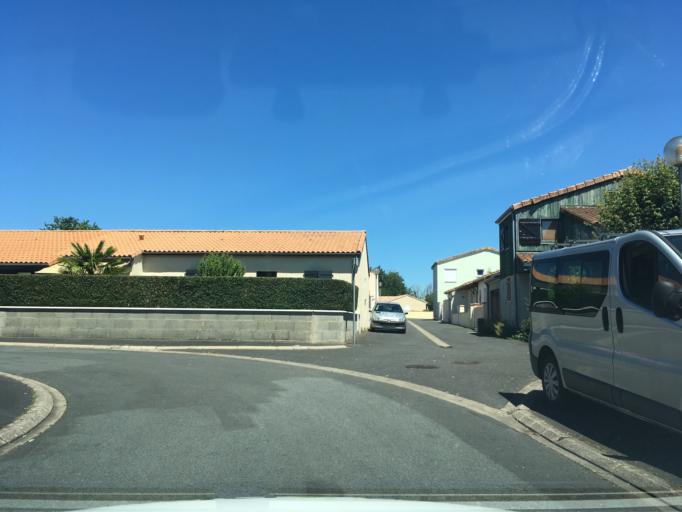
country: FR
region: Poitou-Charentes
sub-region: Departement des Deux-Sevres
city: Niort
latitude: 46.3424
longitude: -0.4399
